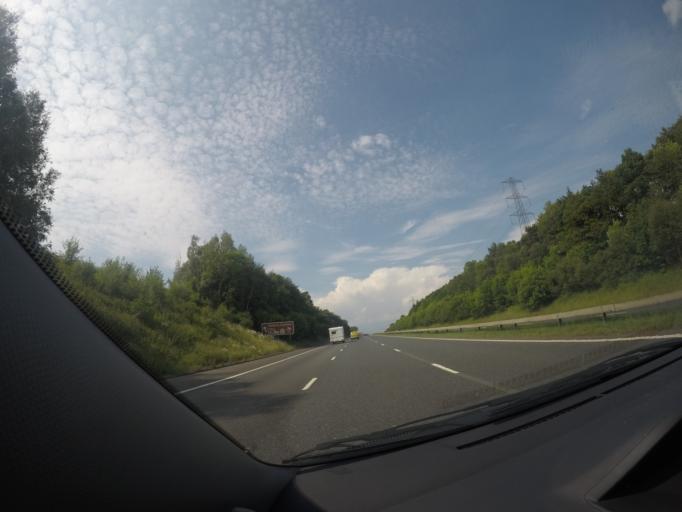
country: GB
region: England
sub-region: Cumbria
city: Scotby
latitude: 54.8802
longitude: -2.8816
